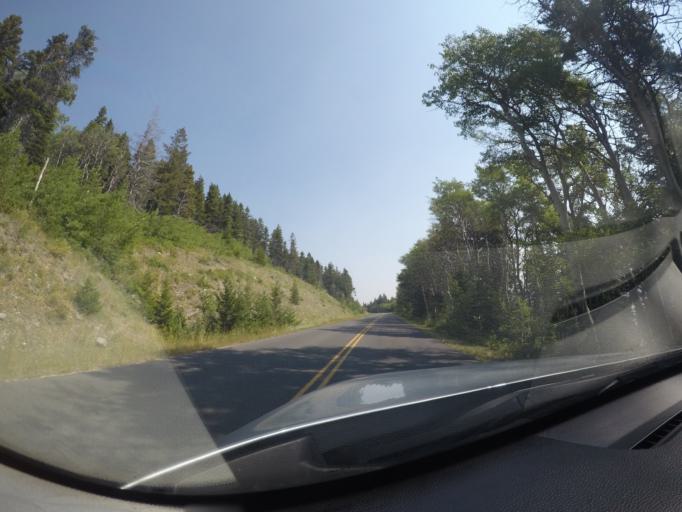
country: US
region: Montana
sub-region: Glacier County
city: Browning
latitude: 48.7051
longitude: -113.4972
